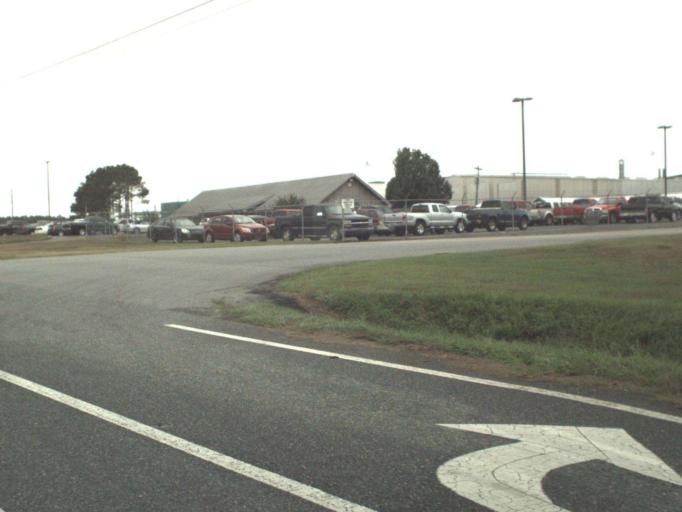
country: US
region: Florida
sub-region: Gadsden County
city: Havana
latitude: 30.6564
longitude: -84.4143
